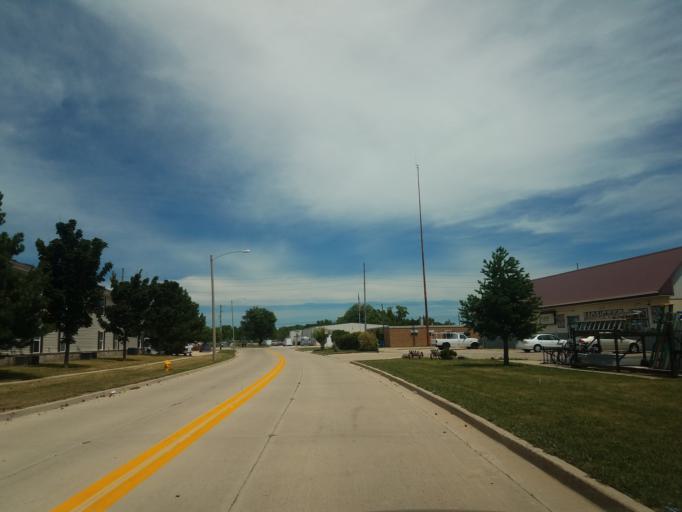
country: US
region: Illinois
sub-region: McLean County
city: Bloomington
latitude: 40.4622
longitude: -88.9883
